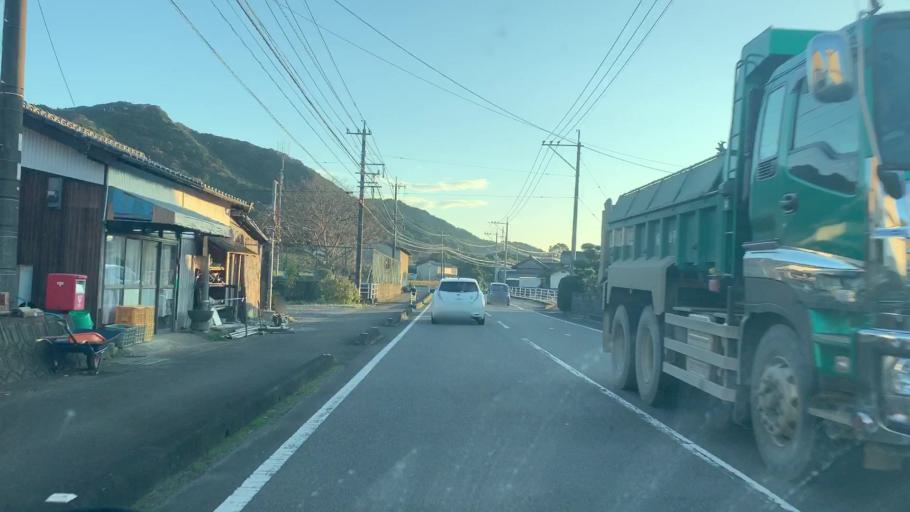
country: JP
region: Saga Prefecture
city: Imaricho-ko
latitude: 33.2844
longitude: 129.9697
